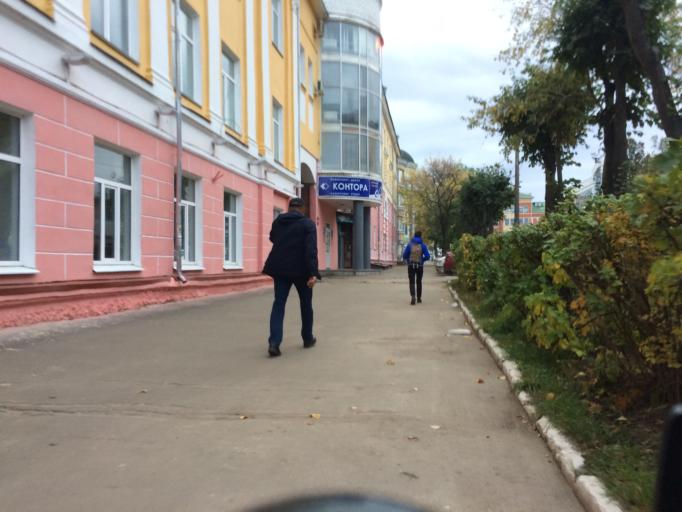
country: RU
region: Mariy-El
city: Yoshkar-Ola
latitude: 56.6336
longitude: 47.8889
